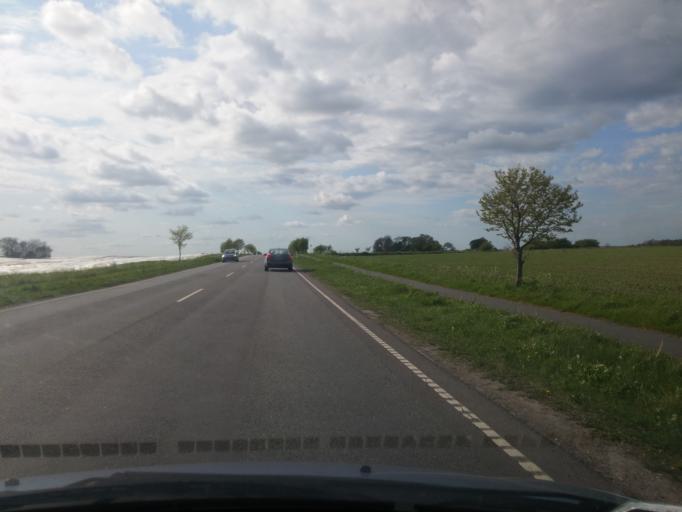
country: DK
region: South Denmark
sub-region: Nyborg Kommune
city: Nyborg
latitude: 55.3223
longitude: 10.7726
